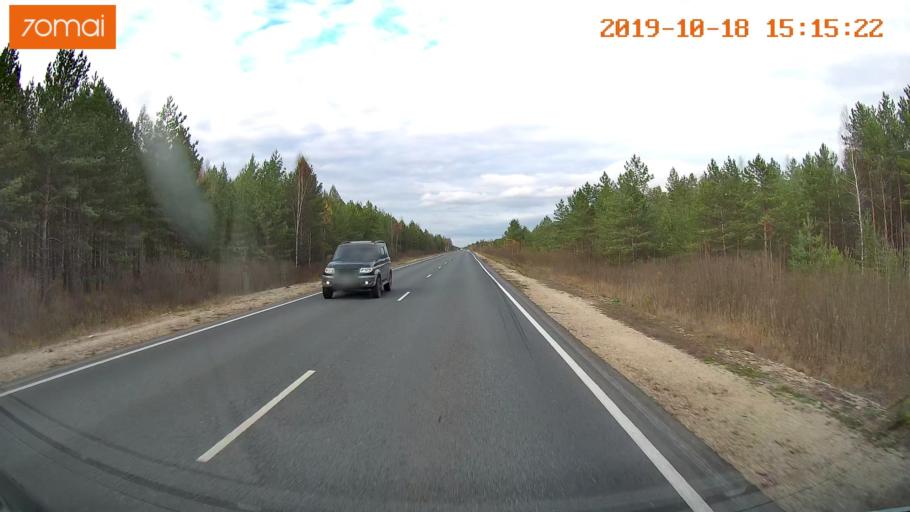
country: RU
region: Vladimir
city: Gus'-Khrustal'nyy
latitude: 55.6177
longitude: 40.7223
